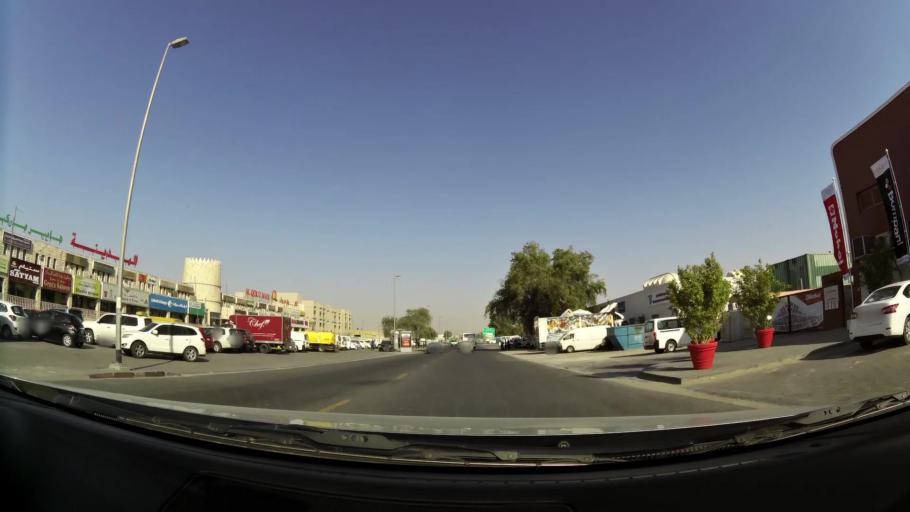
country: AE
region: Dubai
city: Dubai
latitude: 25.1224
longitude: 55.2221
